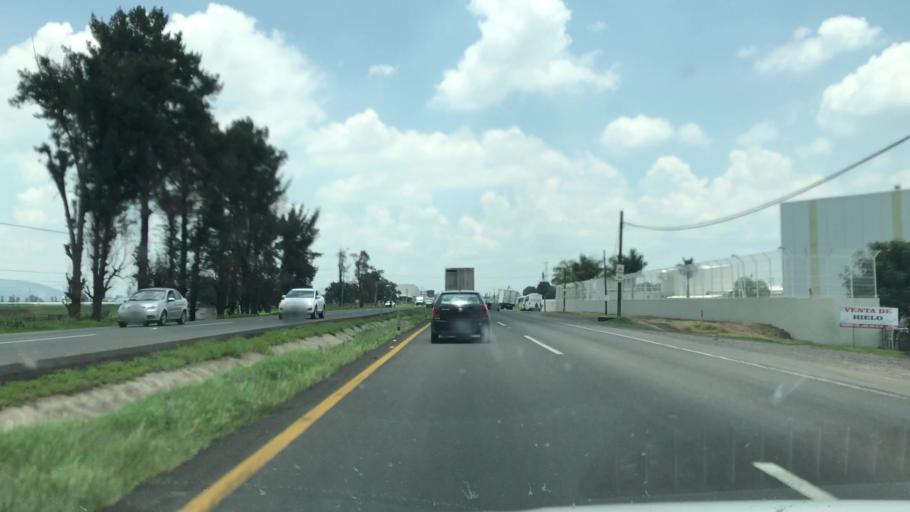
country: MX
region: Guanajuato
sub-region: Irapuato
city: San Jose de Bernalejo (El Guayabo)
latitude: 20.6170
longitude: -101.4029
